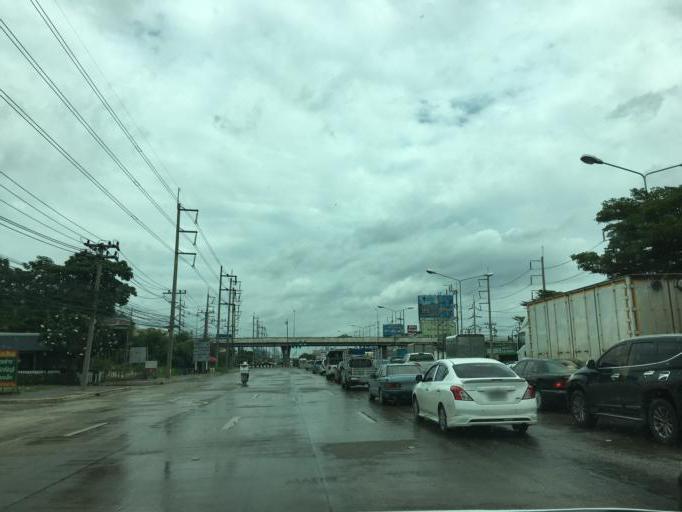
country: TH
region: Phra Nakhon Si Ayutthaya
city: Uthai
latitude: 14.3096
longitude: 100.6442
